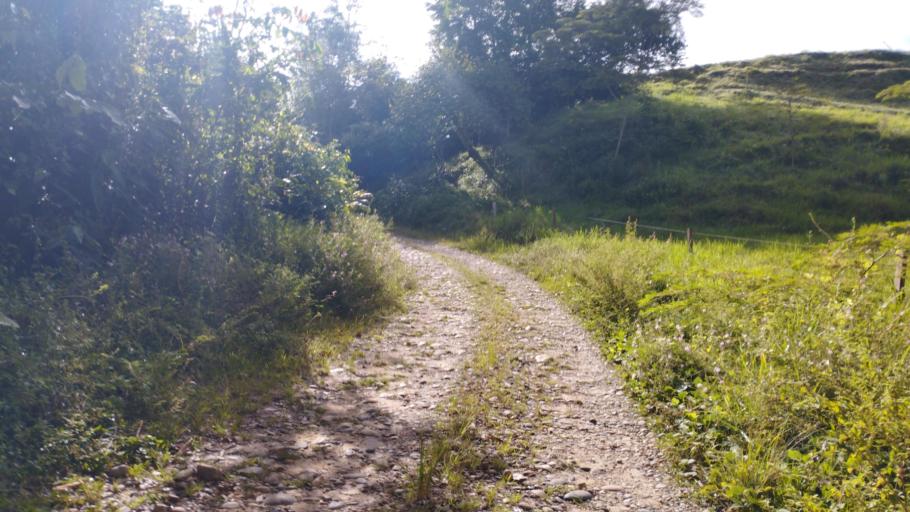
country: CO
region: Casanare
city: Sabanalarga
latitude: 4.7581
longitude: -73.0706
